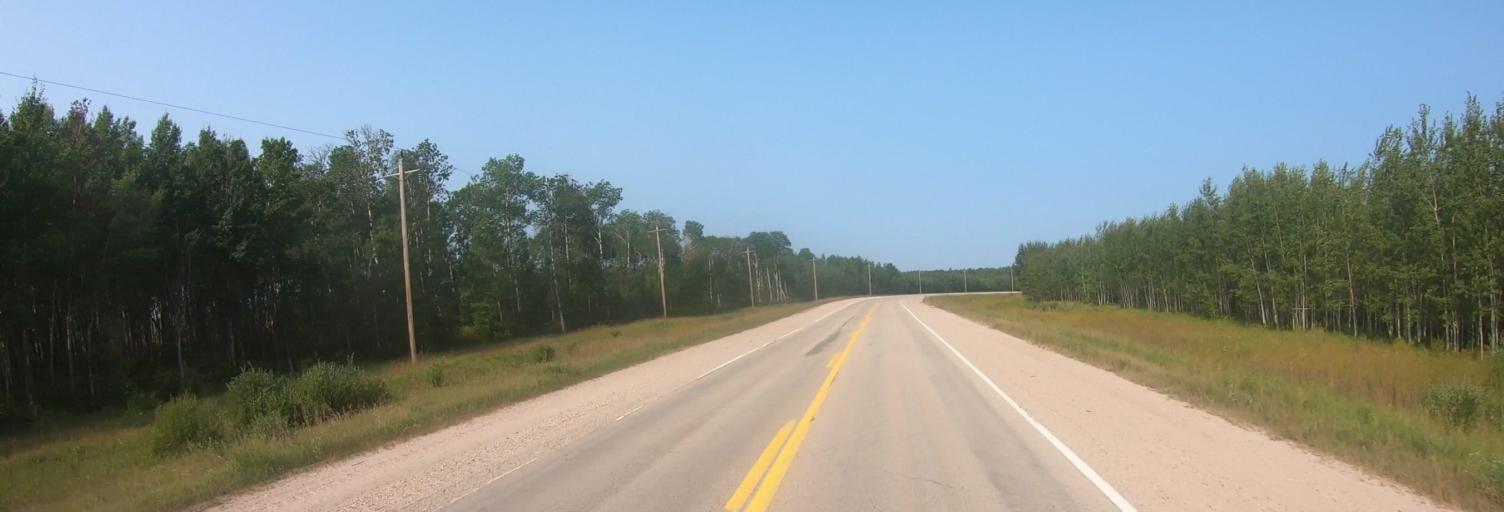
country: US
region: Minnesota
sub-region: Roseau County
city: Roseau
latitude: 49.0233
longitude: -95.7336
